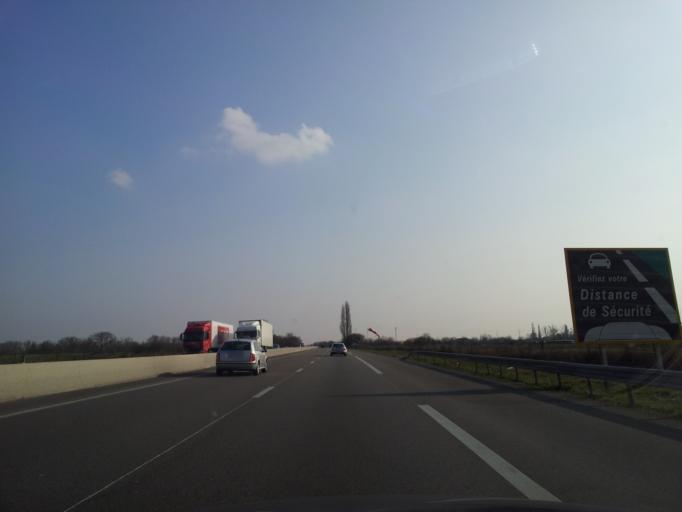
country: FR
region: Alsace
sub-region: Departement du Haut-Rhin
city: Meyenheim
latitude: 47.9214
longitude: 7.3605
